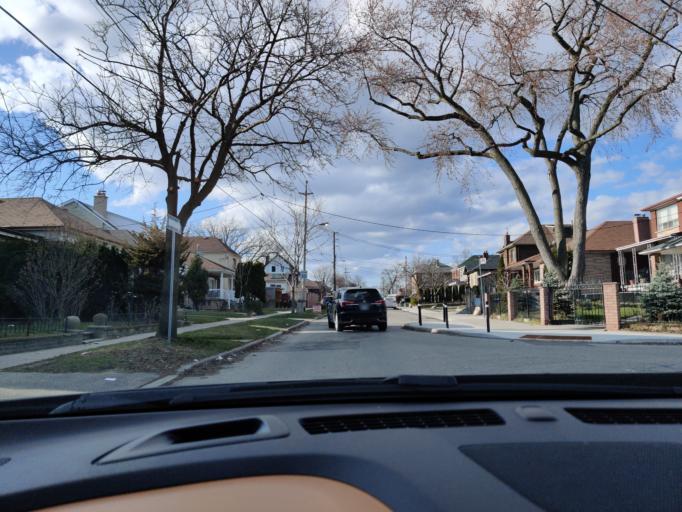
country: CA
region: Ontario
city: Toronto
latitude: 43.6961
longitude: -79.4532
